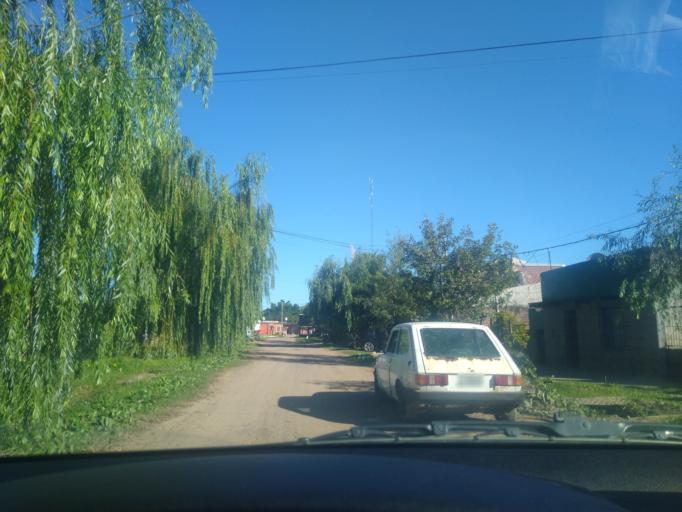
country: AR
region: Chaco
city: Puerto Vilelas
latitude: -27.5159
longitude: -58.9433
